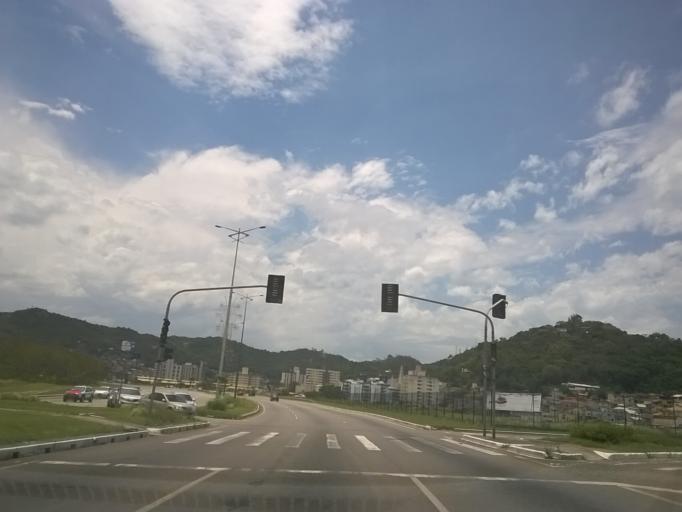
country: BR
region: Santa Catarina
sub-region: Florianopolis
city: Saco dos Limoes
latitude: -27.6159
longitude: -48.5286
